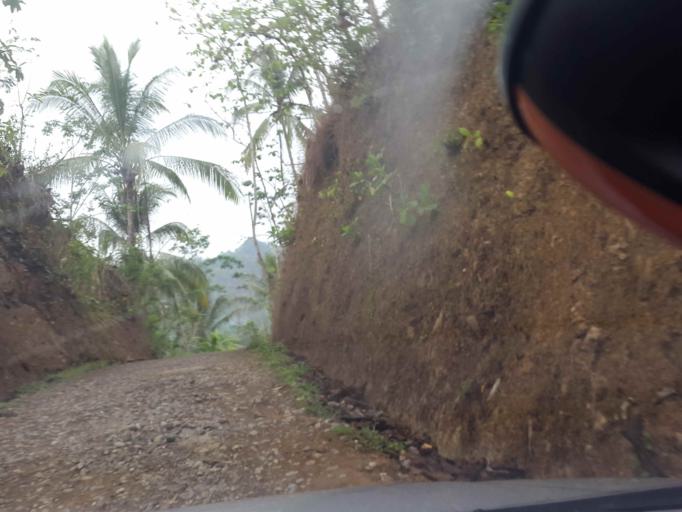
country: ID
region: East Java
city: Sudimoro
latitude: -8.2011
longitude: 111.3289
